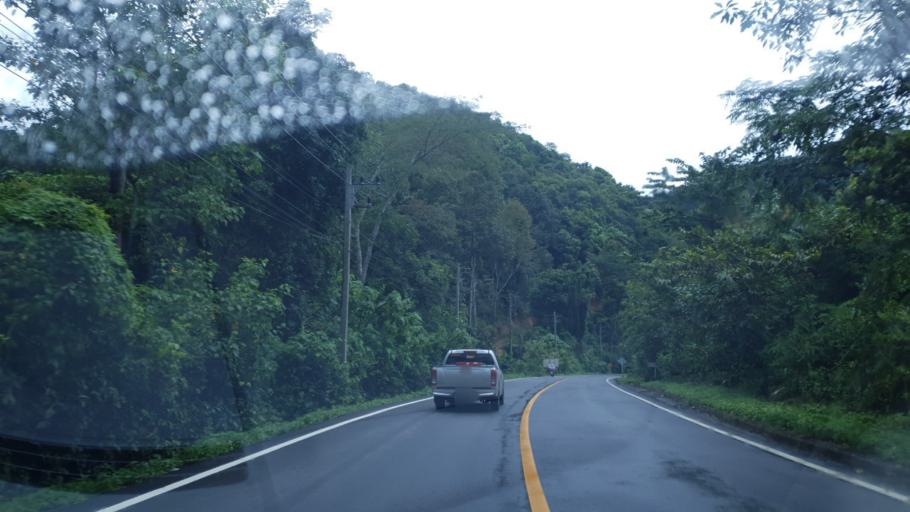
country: TH
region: Mae Hong Son
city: Ban Huai I Huak
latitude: 18.1469
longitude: 98.0938
